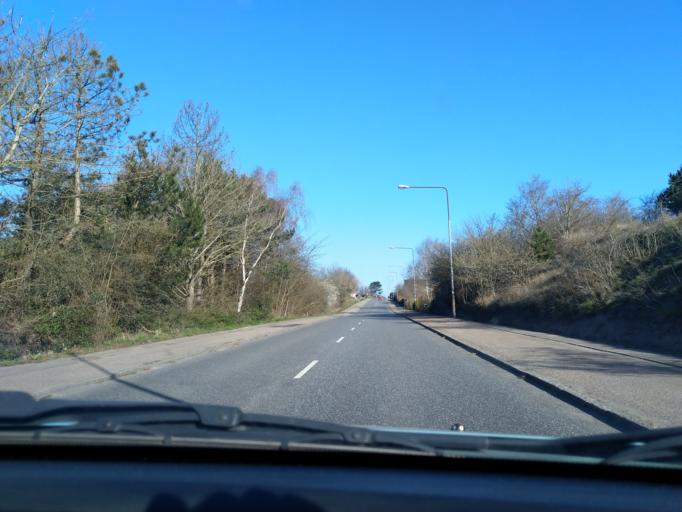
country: DK
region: Zealand
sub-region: Kalundborg Kommune
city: Kalundborg
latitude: 55.7056
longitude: 11.0232
